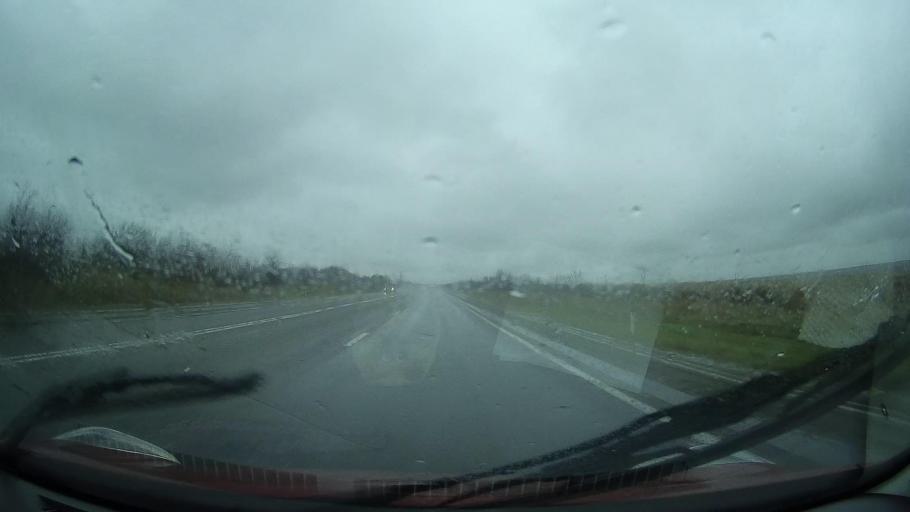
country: RU
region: Stavropol'skiy
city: Nevinnomyssk
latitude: 44.6324
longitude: 42.0180
